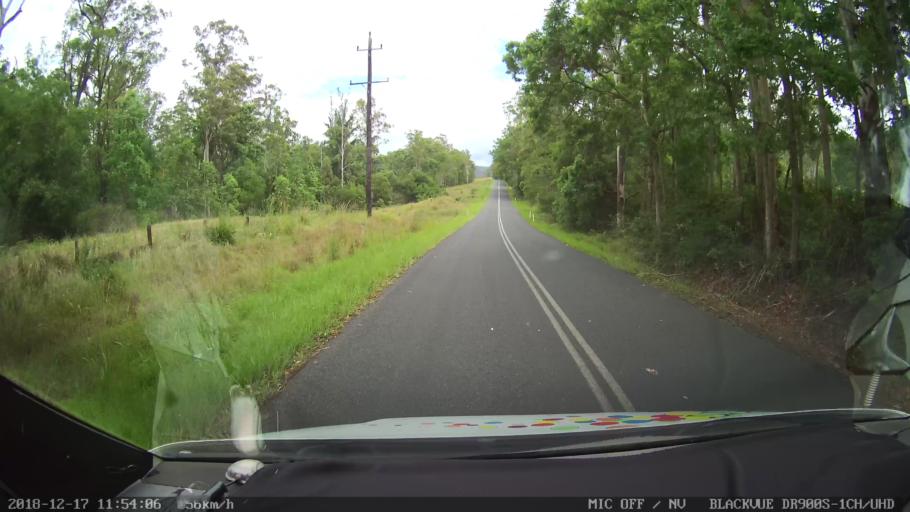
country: AU
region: New South Wales
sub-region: Kyogle
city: Kyogle
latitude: -28.5696
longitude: 152.5847
